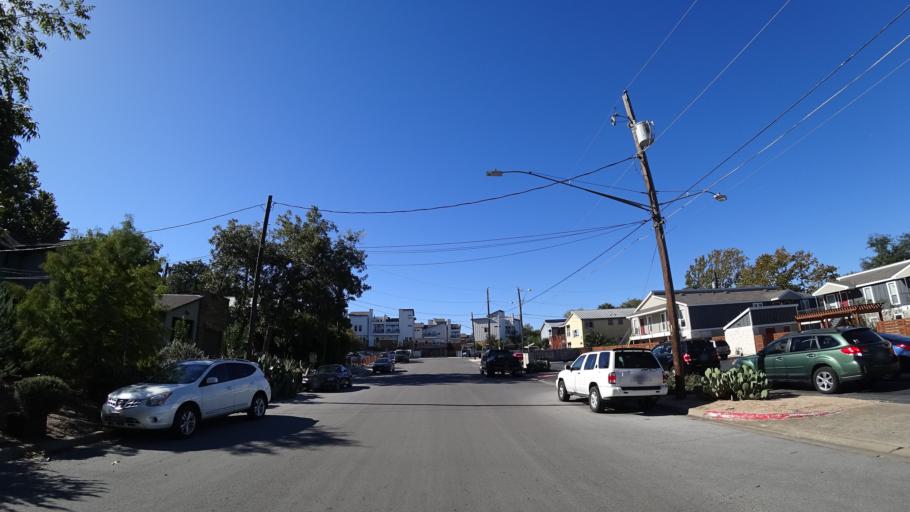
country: US
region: Texas
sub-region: Travis County
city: Austin
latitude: 30.2394
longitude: -97.7590
